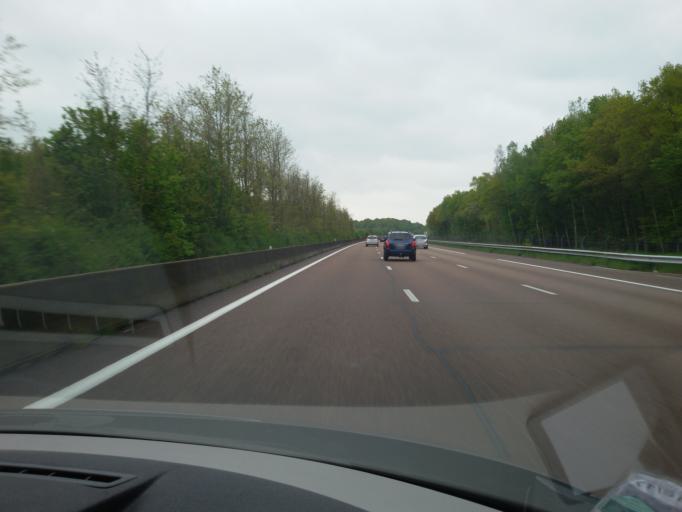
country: FR
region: Bourgogne
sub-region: Departement de Saone-et-Loire
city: Champforgeuil
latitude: 46.8697
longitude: 4.8197
